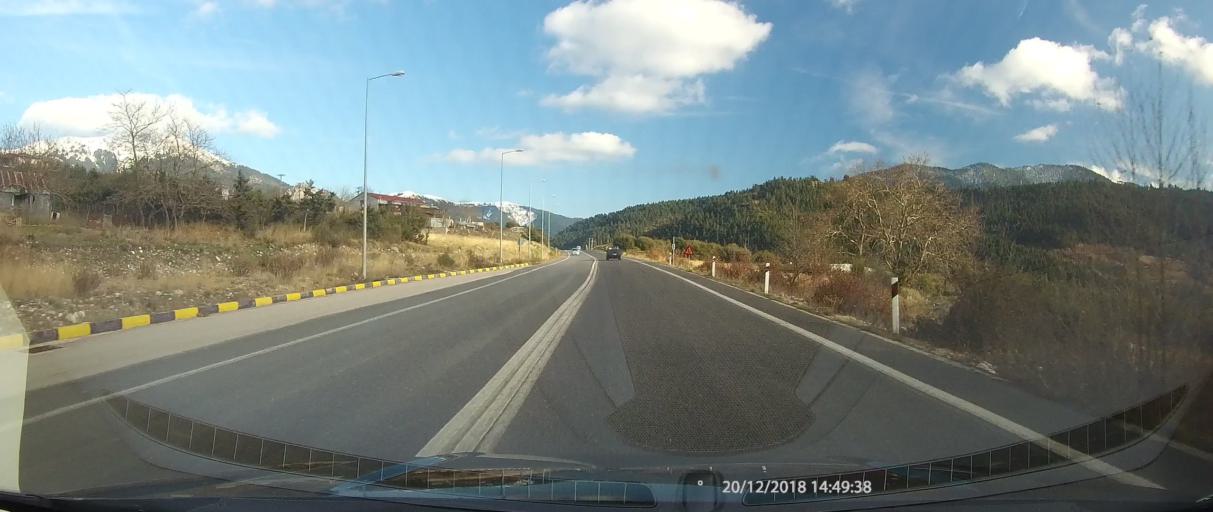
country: GR
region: Central Greece
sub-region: Nomos Evrytanias
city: Karpenisi
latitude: 38.9044
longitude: 21.8081
